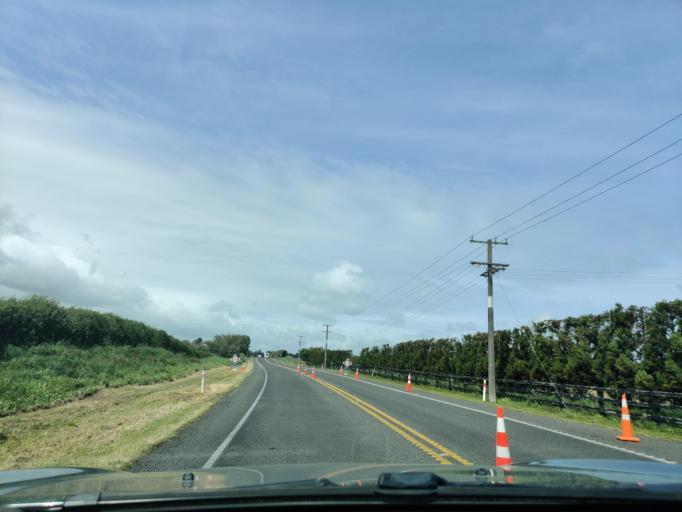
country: NZ
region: Taranaki
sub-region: South Taranaki District
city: Hawera
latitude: -39.6202
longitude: 174.3527
